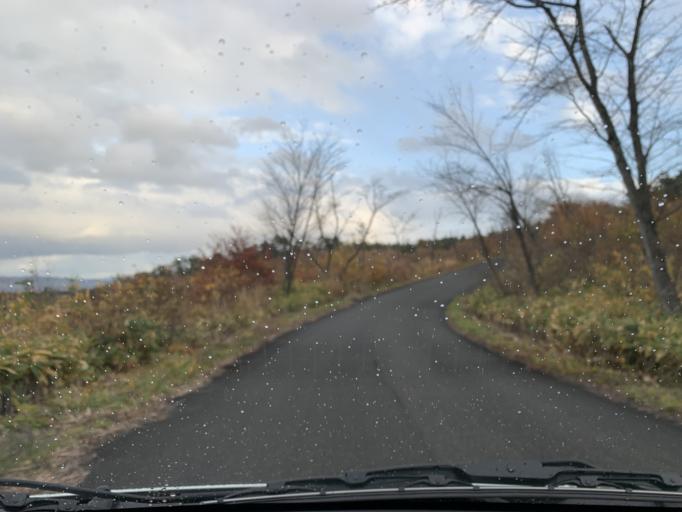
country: JP
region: Iwate
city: Mizusawa
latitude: 39.0805
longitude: 141.0223
